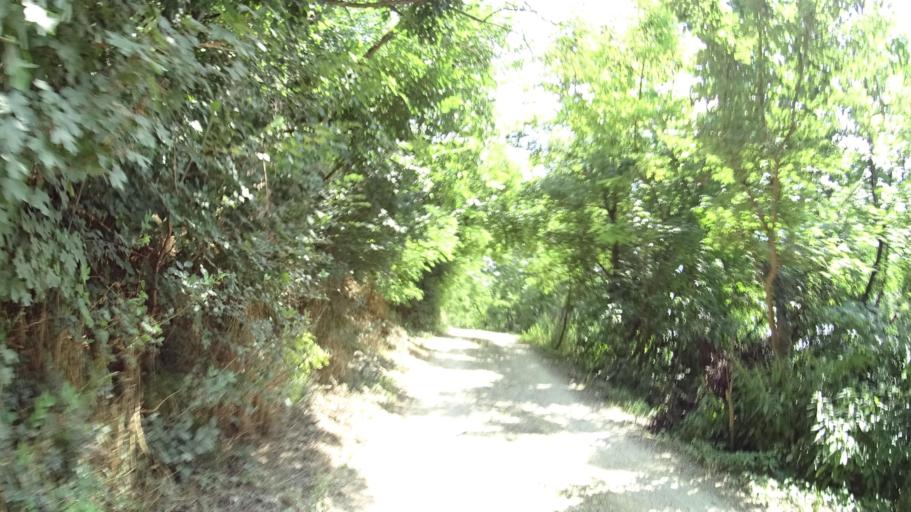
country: HU
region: Veszprem
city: Tihany
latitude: 46.8901
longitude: 17.8774
